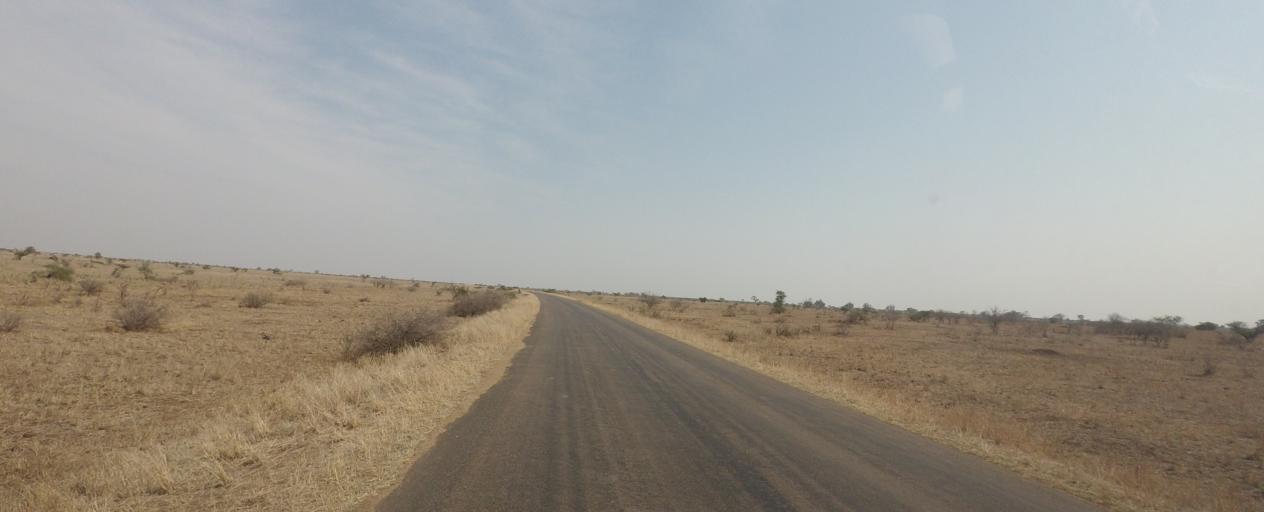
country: ZA
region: Limpopo
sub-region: Mopani District Municipality
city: Phalaborwa
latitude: -24.2766
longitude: 31.7376
